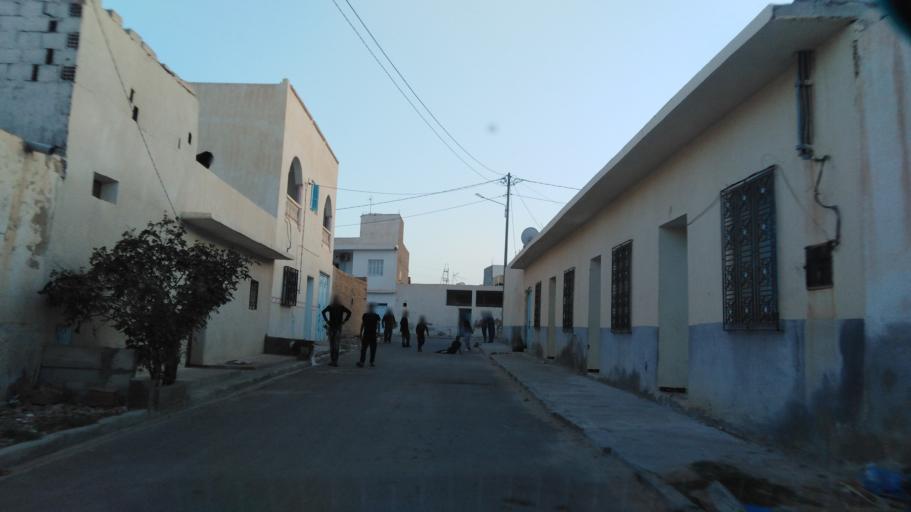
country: TN
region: Tataouine
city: Tataouine
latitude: 32.9381
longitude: 10.4560
